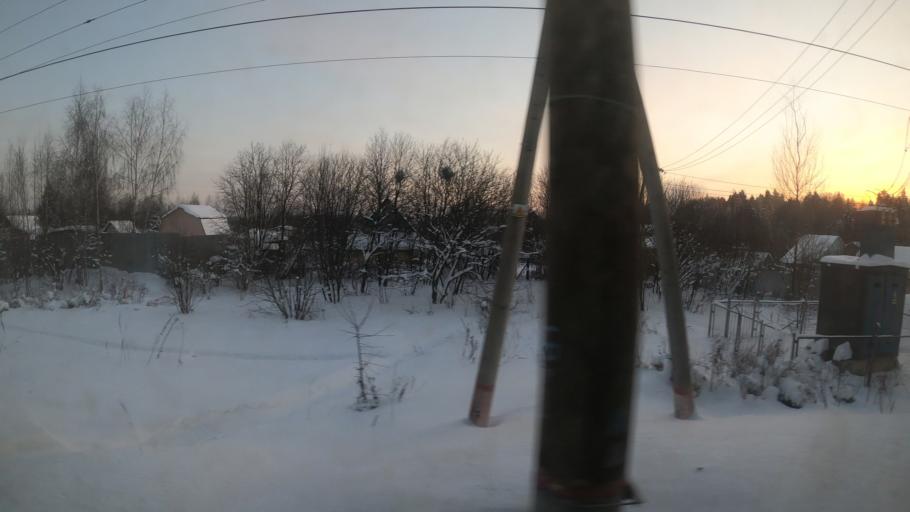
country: RU
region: Moskovskaya
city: Yermolino
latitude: 56.1410
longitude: 37.5064
